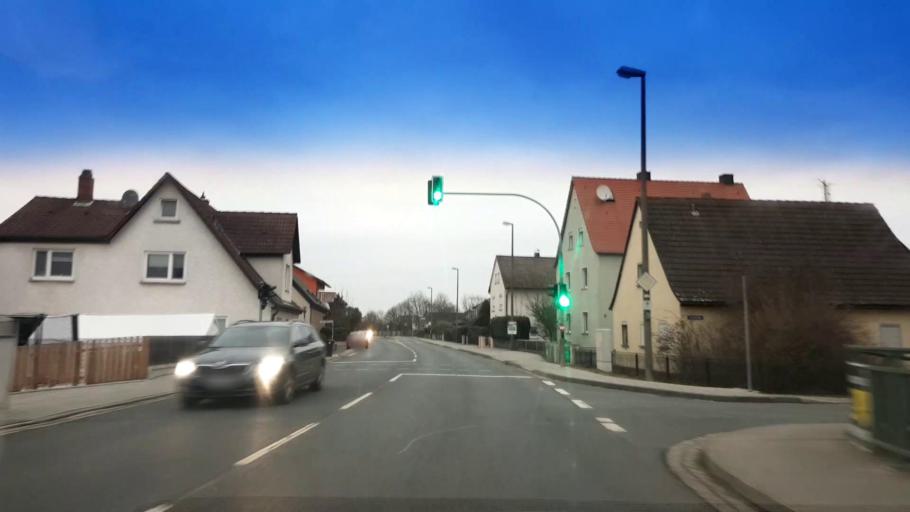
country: DE
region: Bavaria
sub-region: Upper Franconia
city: Altendorf
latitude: 49.7979
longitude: 11.0104
